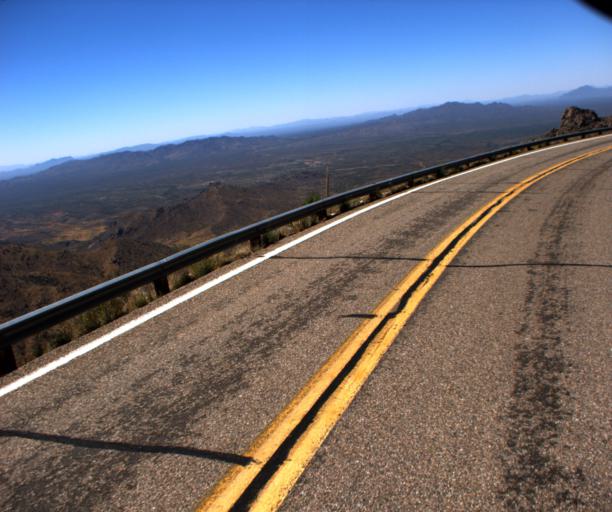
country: US
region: Arizona
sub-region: Pima County
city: Sells
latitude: 31.9512
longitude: -111.6273
